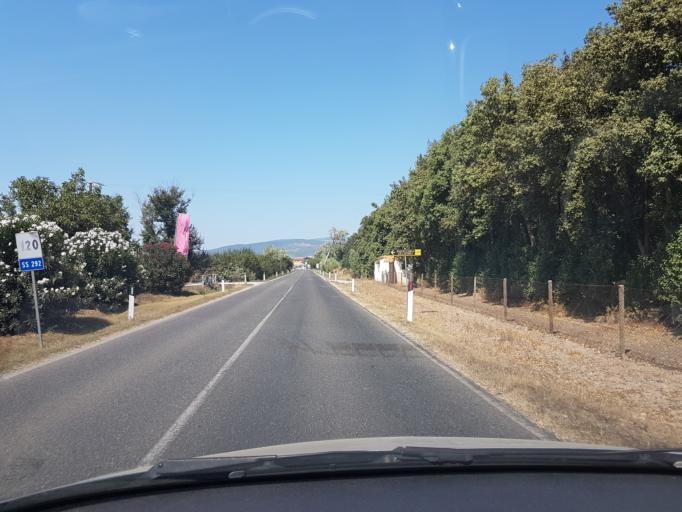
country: IT
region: Sardinia
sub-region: Provincia di Oristano
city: Riola Sardo
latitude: 39.9851
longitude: 8.5401
